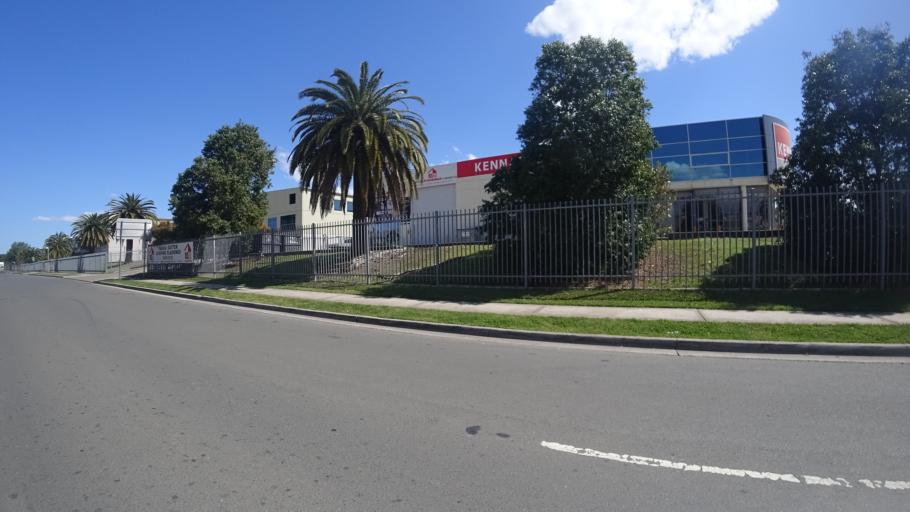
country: AU
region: New South Wales
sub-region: Liverpool
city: Miller
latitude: -33.9283
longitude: 150.8825
